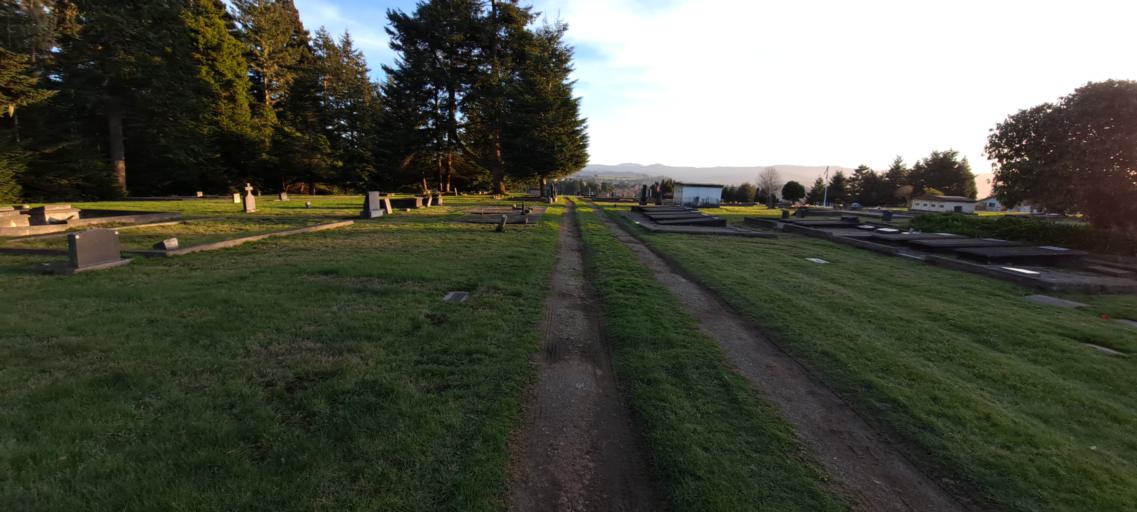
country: US
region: California
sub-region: Humboldt County
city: Fortuna
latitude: 40.5982
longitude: -124.1313
